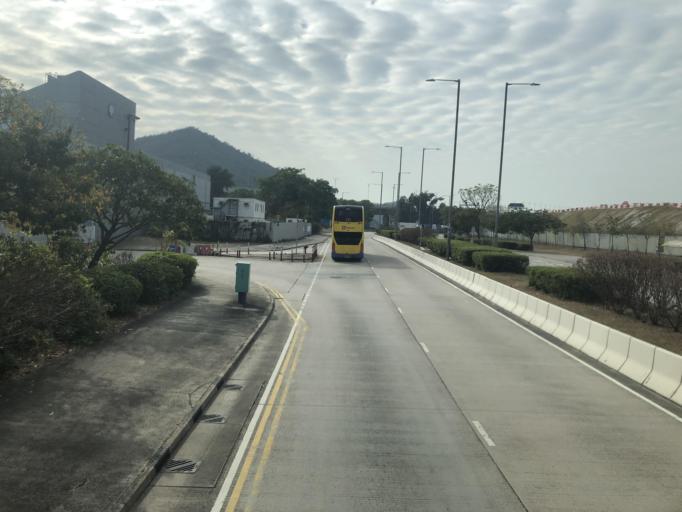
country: HK
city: Tai O
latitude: 22.2949
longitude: 113.9238
